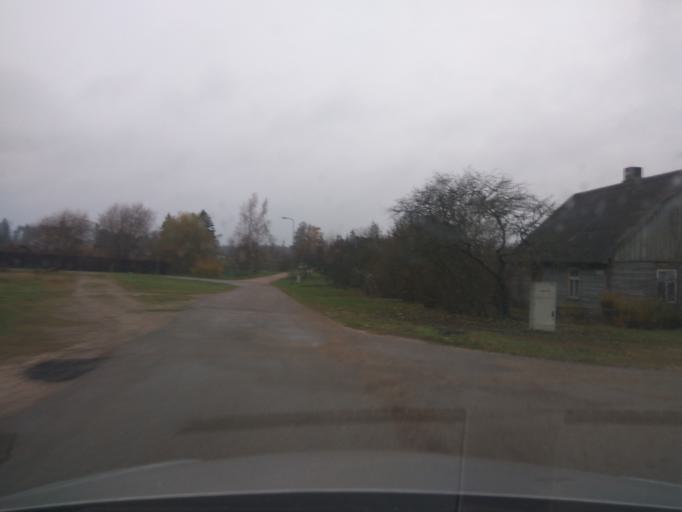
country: LV
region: Kuldigas Rajons
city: Kuldiga
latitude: 56.9223
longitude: 21.9667
